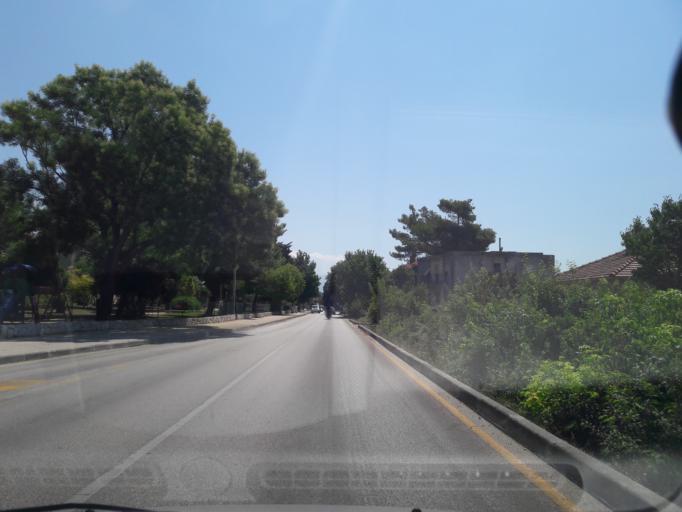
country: HR
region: Splitsko-Dalmatinska
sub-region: Grad Split
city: Split
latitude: 43.5481
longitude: 16.4011
